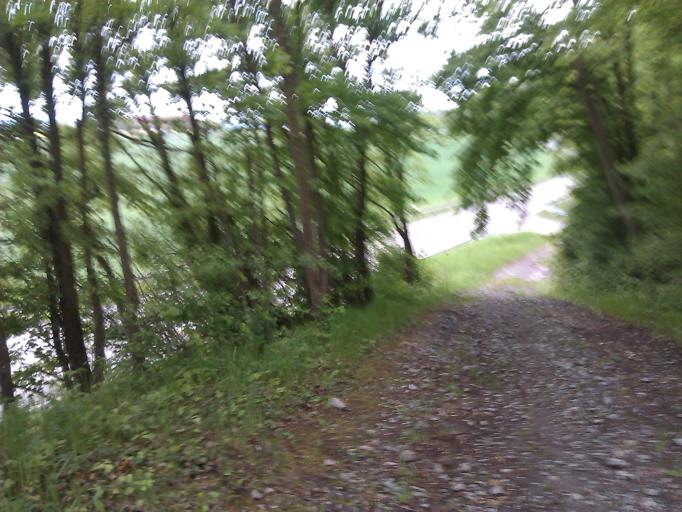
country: DE
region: Baden-Wuerttemberg
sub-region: Karlsruhe Region
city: Knittlingen
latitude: 49.0502
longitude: 8.7618
